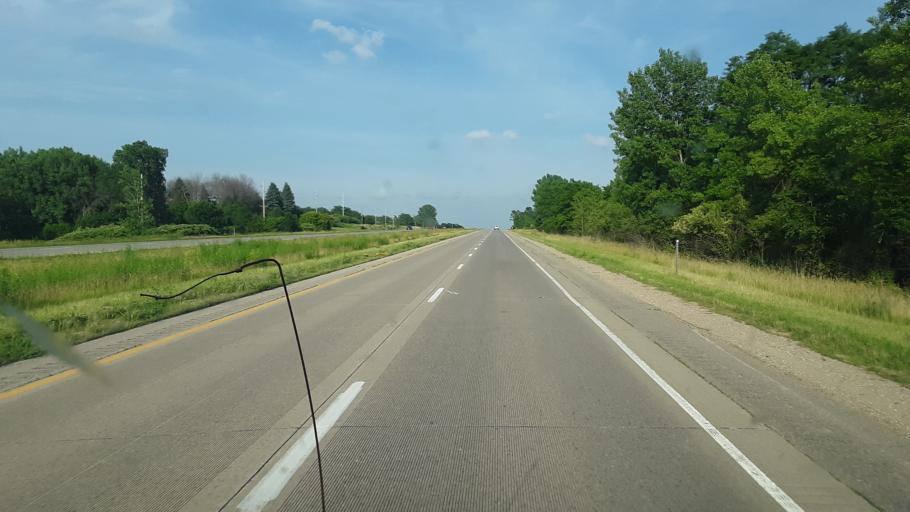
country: US
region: Iowa
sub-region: Tama County
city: Toledo
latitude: 42.0061
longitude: -92.7448
